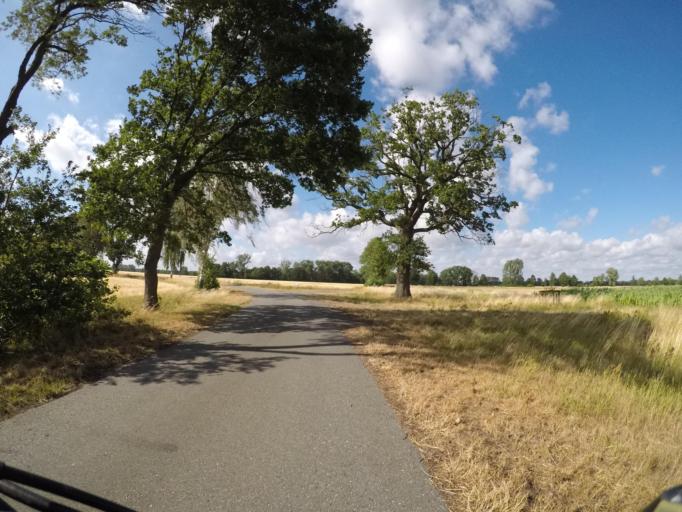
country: DE
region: Lower Saxony
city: Damnatz
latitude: 53.1807
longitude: 11.1699
